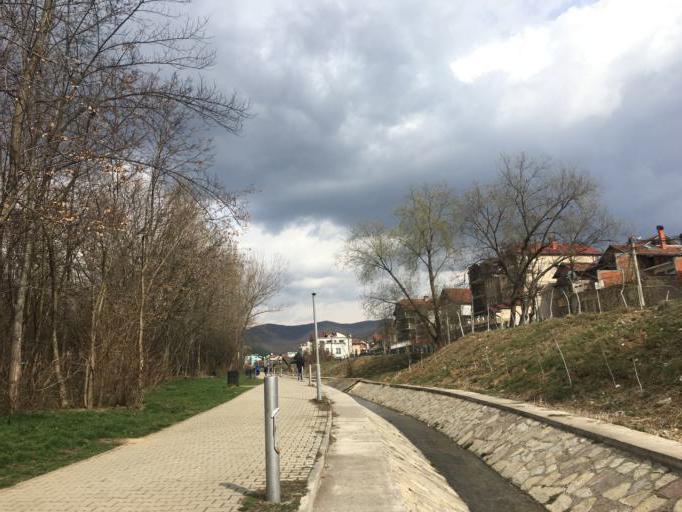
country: XK
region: Pristina
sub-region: Komuna e Prishtines
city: Pristina
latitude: 42.6662
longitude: 21.1861
